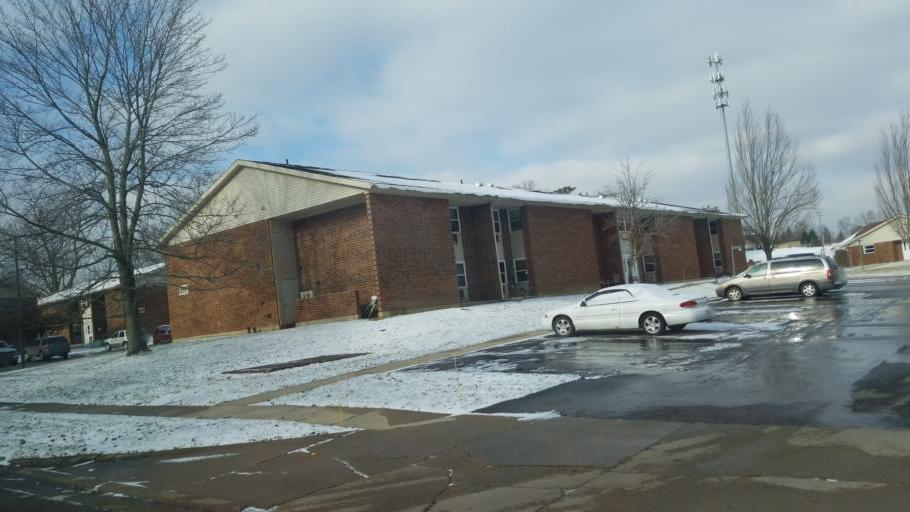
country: US
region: Ohio
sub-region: Richland County
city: Mansfield
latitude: 40.7340
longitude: -82.5288
